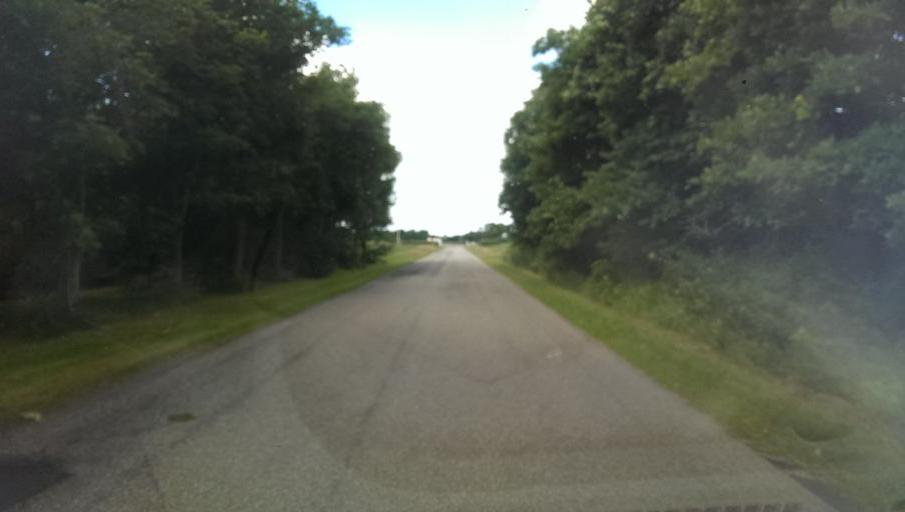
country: DK
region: Central Jutland
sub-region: Holstebro Kommune
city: Ulfborg
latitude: 56.2596
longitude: 8.2393
